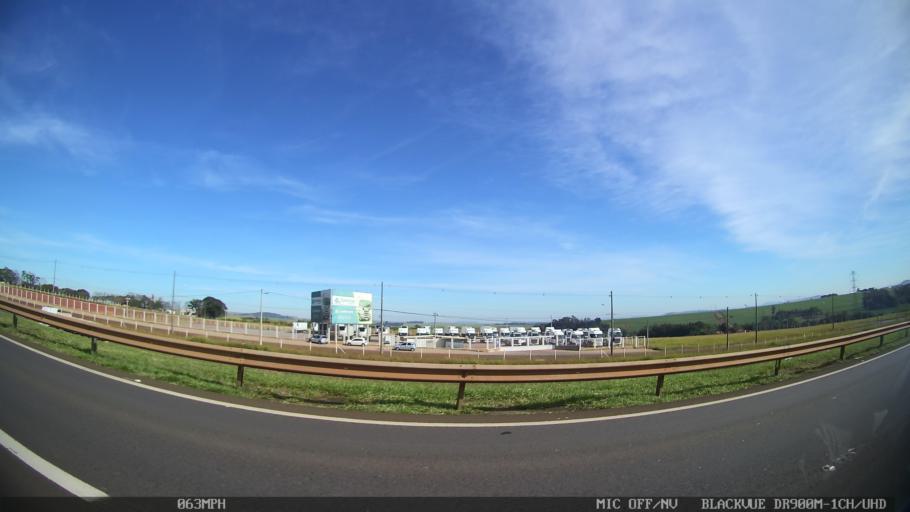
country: BR
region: Sao Paulo
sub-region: Araras
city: Araras
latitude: -22.4028
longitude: -47.3895
